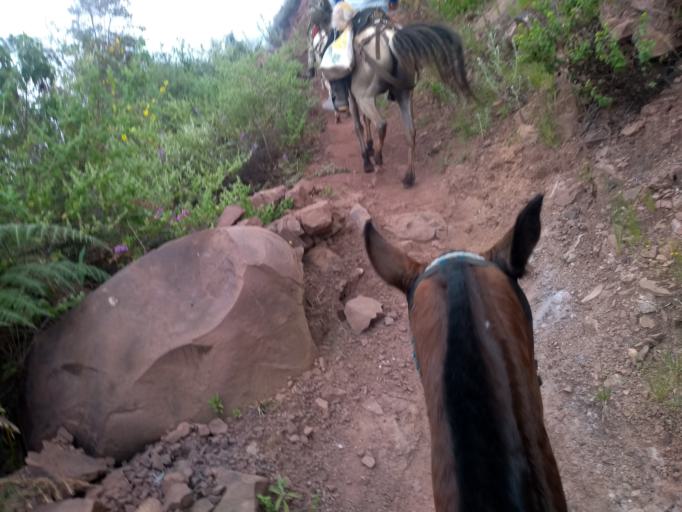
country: CO
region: Cesar
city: San Diego
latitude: 10.1791
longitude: -73.0424
